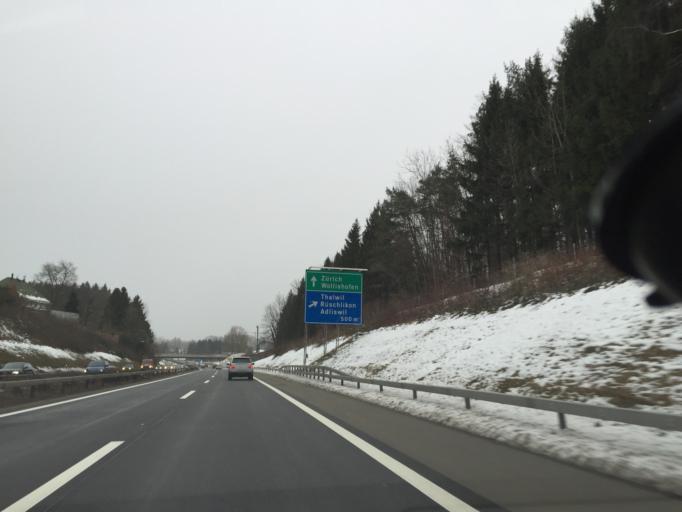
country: CH
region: Zurich
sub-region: Bezirk Horgen
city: Thalwil / Nord
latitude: 47.2953
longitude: 8.5497
